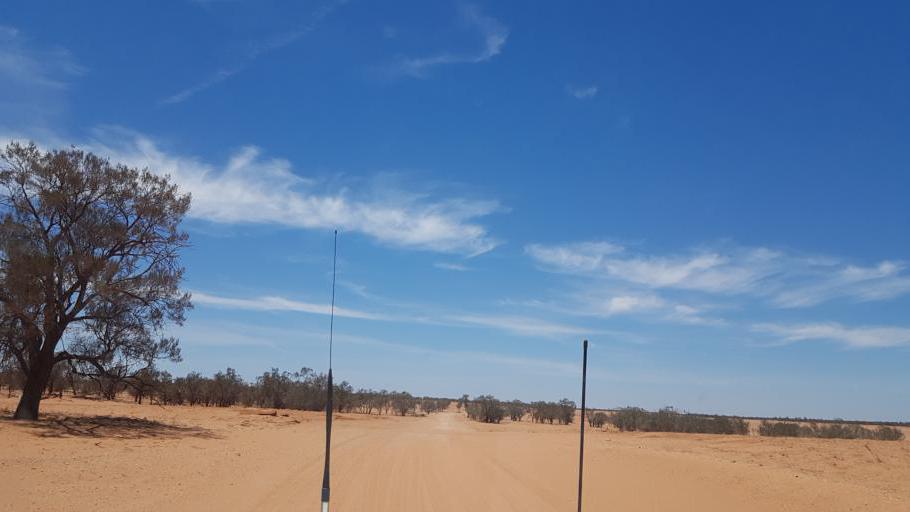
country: AU
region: New South Wales
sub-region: Wentworth
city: Dareton
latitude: -33.3463
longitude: 141.4609
